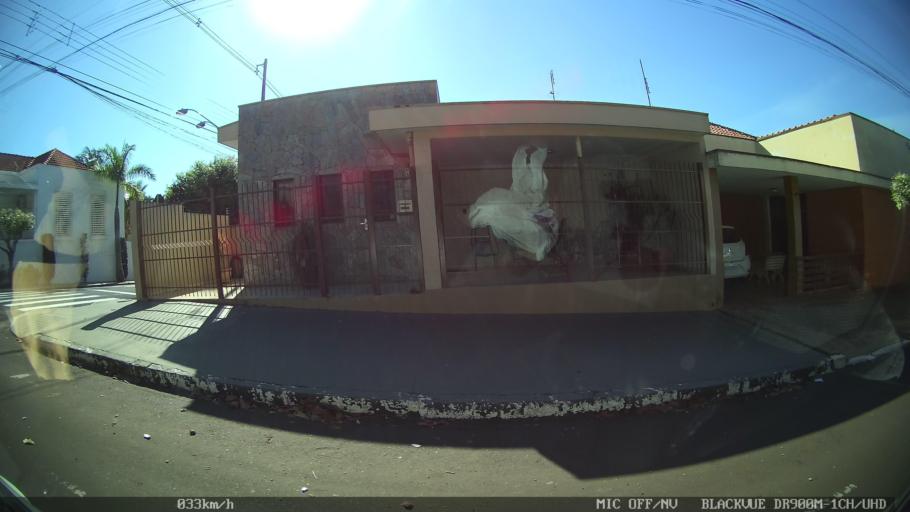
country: BR
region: Sao Paulo
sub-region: Olimpia
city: Olimpia
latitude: -20.7414
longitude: -48.9143
